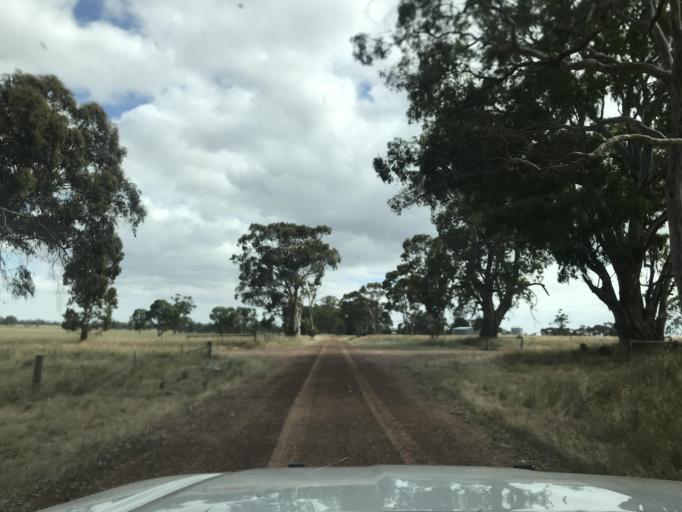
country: AU
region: South Australia
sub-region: Naracoorte and Lucindale
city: Naracoorte
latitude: -36.9005
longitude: 141.4016
